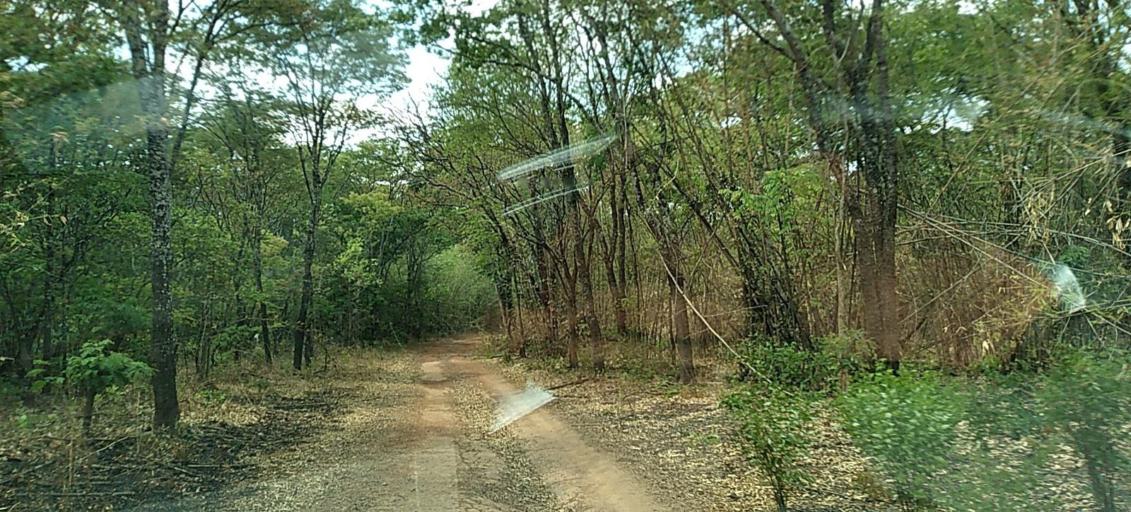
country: ZM
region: Copperbelt
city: Chililabombwe
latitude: -12.4798
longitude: 27.6445
